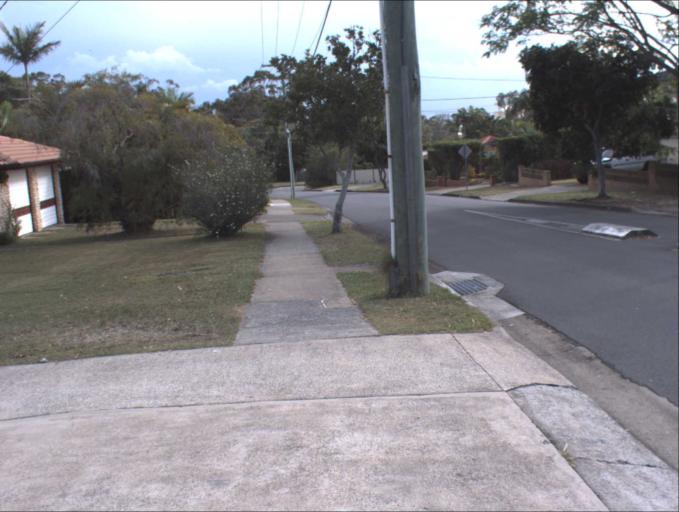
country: AU
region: Queensland
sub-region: Logan
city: Springwood
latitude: -27.6130
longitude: 153.1317
